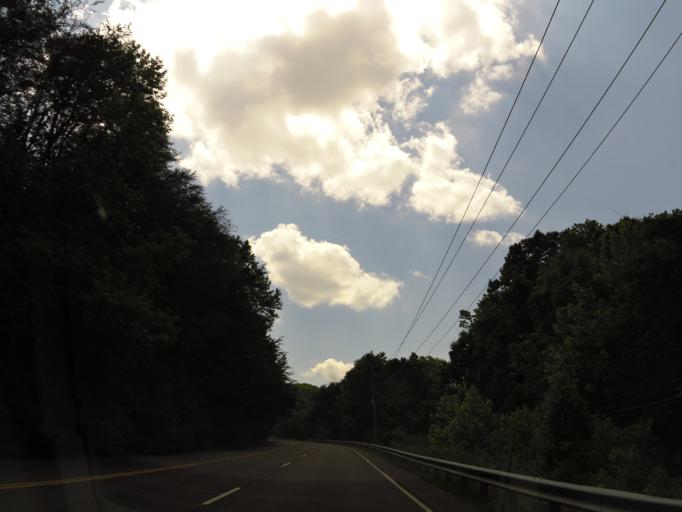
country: US
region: Tennessee
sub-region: Rhea County
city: Dayton
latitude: 35.5024
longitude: -85.0349
